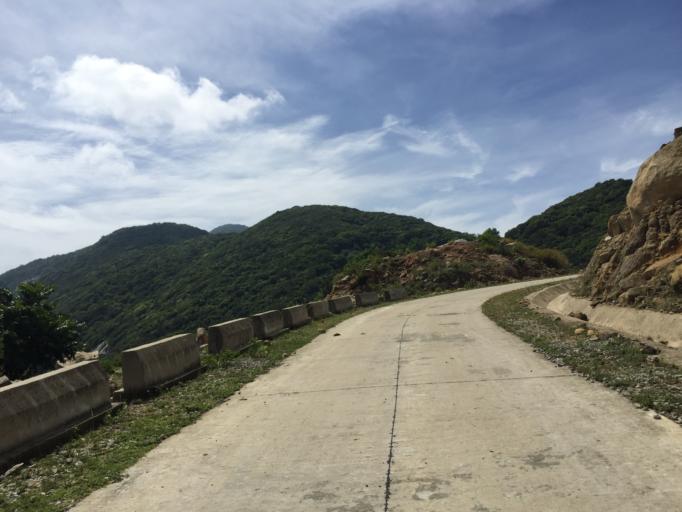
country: VN
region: Quang Nam
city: Hoi An
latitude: 15.9652
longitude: 108.5097
